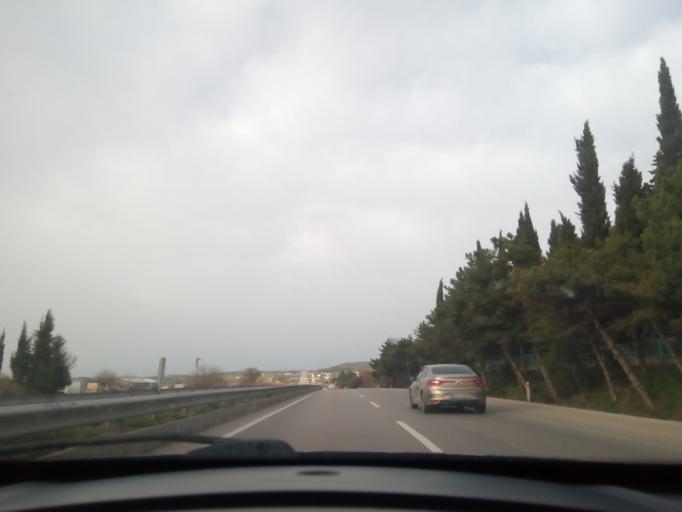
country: TR
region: Bursa
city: Gorukle
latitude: 40.2145
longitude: 28.7228
